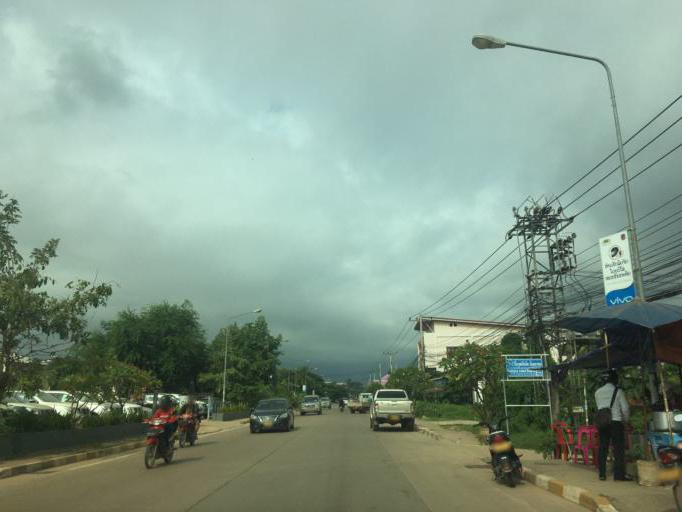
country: TH
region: Nong Khai
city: Si Chiang Mai
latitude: 17.9754
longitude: 102.5462
